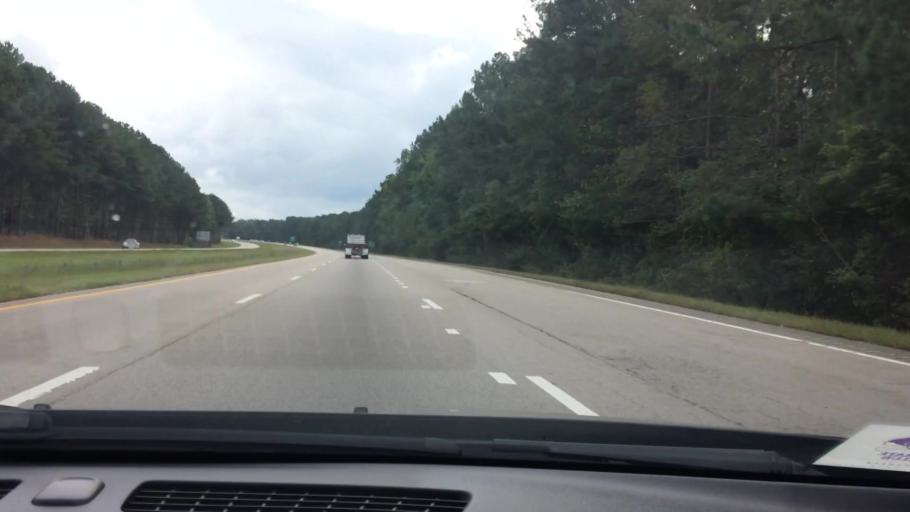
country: US
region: North Carolina
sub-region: Wake County
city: Zebulon
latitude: 35.8271
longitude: -78.2868
